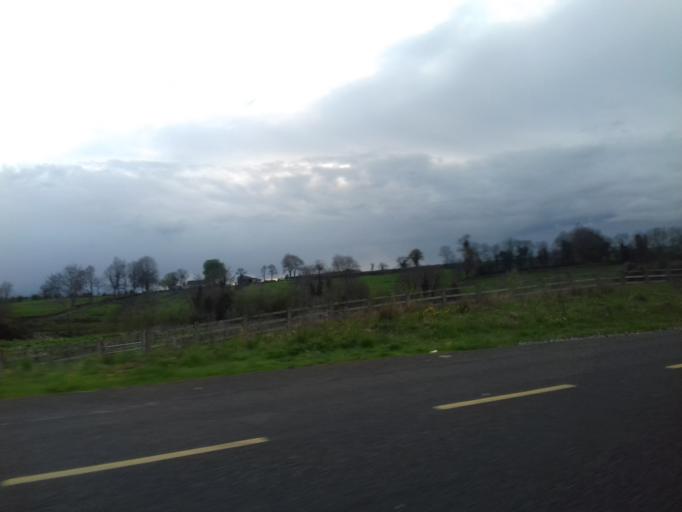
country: IE
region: Ulster
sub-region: An Cabhan
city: Belturbet
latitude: 54.0889
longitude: -7.4506
